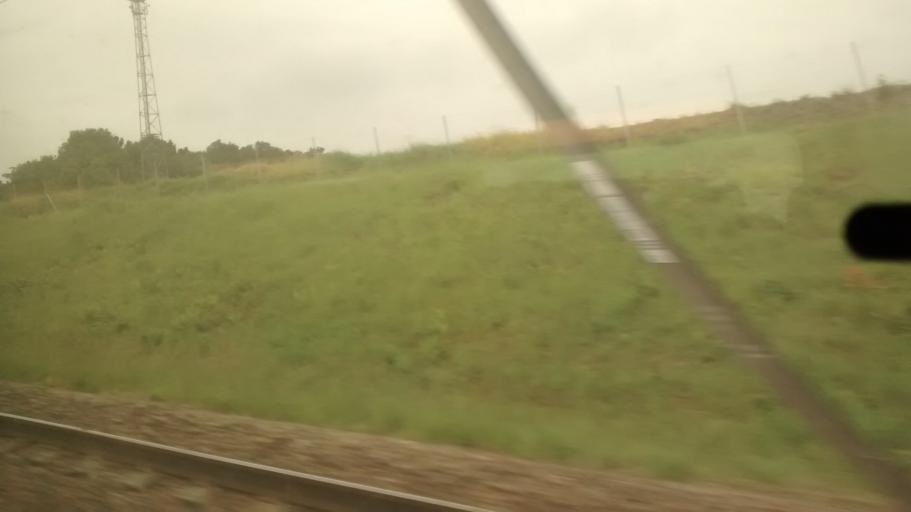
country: FR
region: Ile-de-France
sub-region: Departement de Seine-et-Marne
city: Moisenay
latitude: 48.5570
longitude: 2.7683
